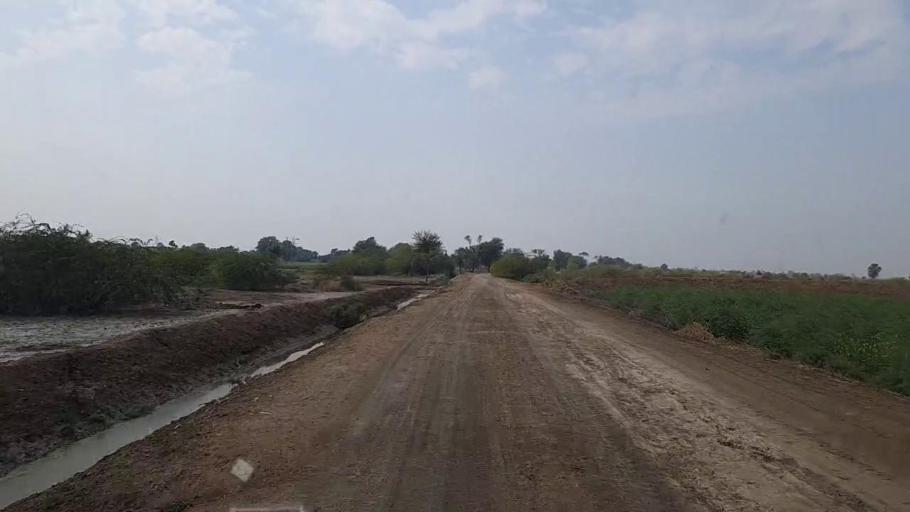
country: PK
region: Sindh
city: Mirwah Gorchani
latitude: 25.3485
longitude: 69.0744
